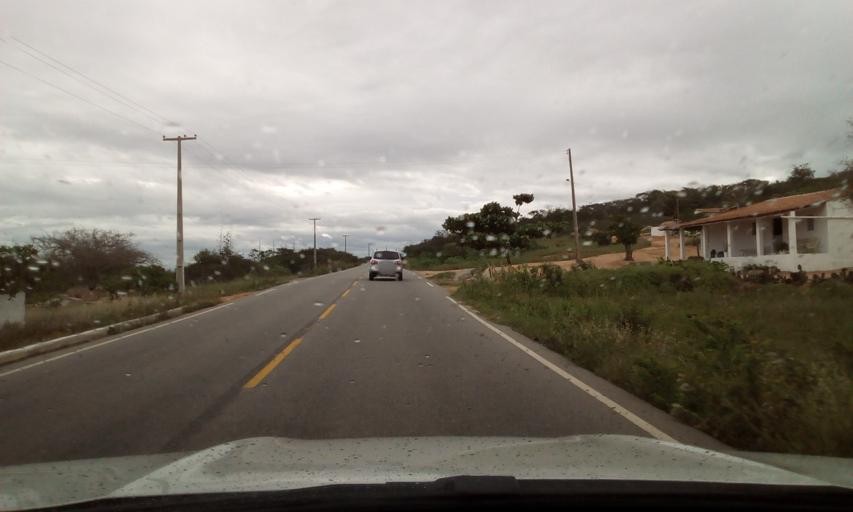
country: BR
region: Paraiba
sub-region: Picui
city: Picui
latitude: -6.5736
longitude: -36.2670
